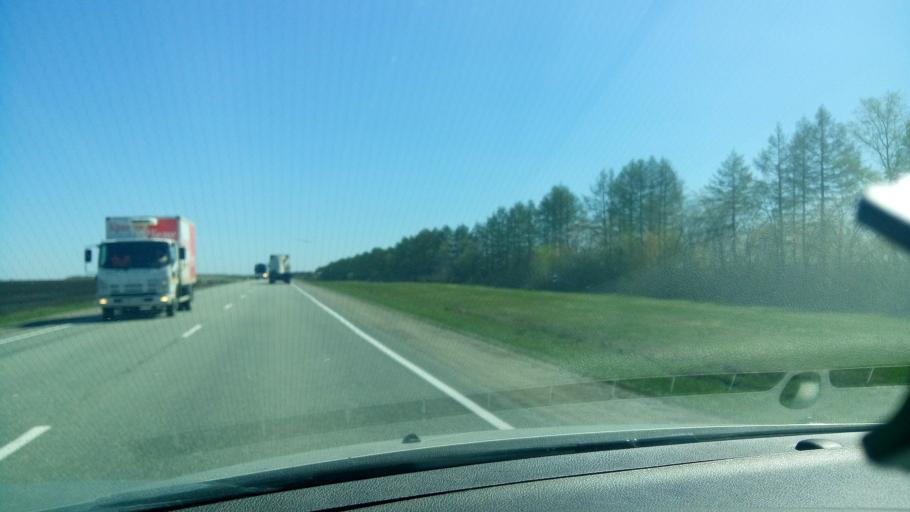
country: RU
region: Sverdlovsk
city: Yelanskiy
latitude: 56.7811
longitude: 62.4896
